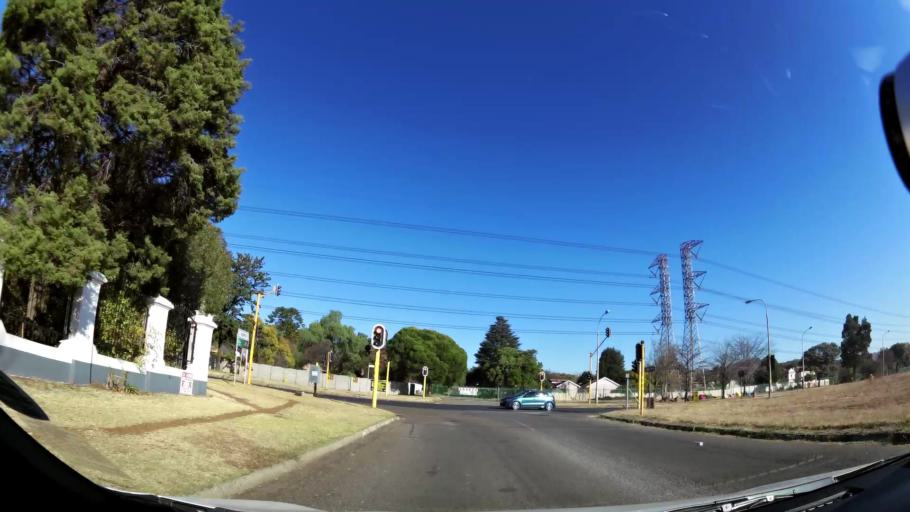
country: ZA
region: Gauteng
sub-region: Ekurhuleni Metropolitan Municipality
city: Germiston
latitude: -26.2817
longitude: 28.1110
